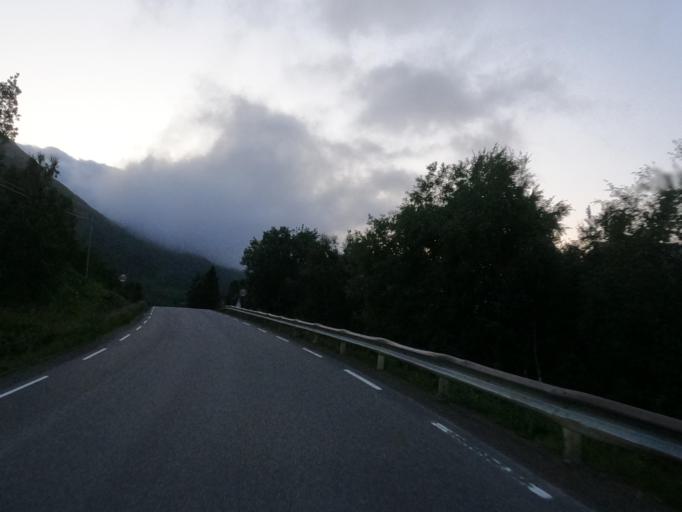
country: NO
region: Nordland
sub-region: Lodingen
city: Lodingen
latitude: 68.5660
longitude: 15.8013
